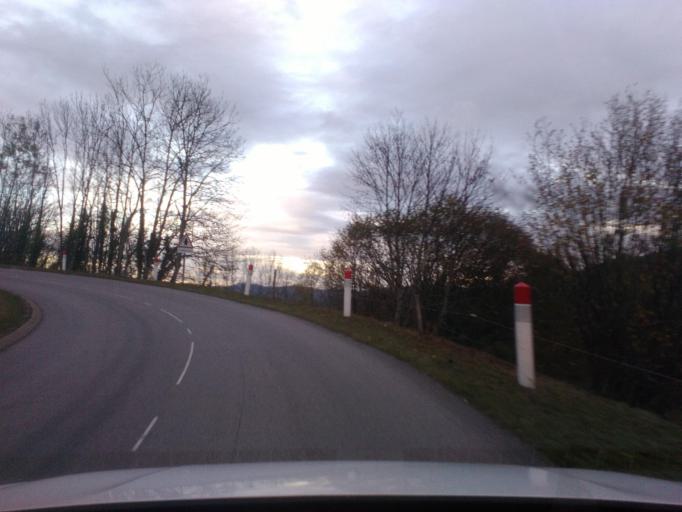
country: FR
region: Lorraine
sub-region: Departement des Vosges
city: Plainfaing
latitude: 48.2042
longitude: 7.0347
